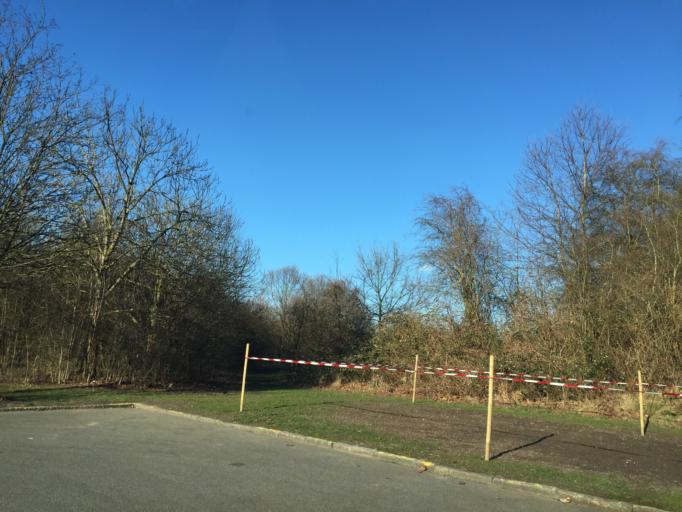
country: DK
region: South Denmark
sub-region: Odense Kommune
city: Odense
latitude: 55.3765
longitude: 10.3988
